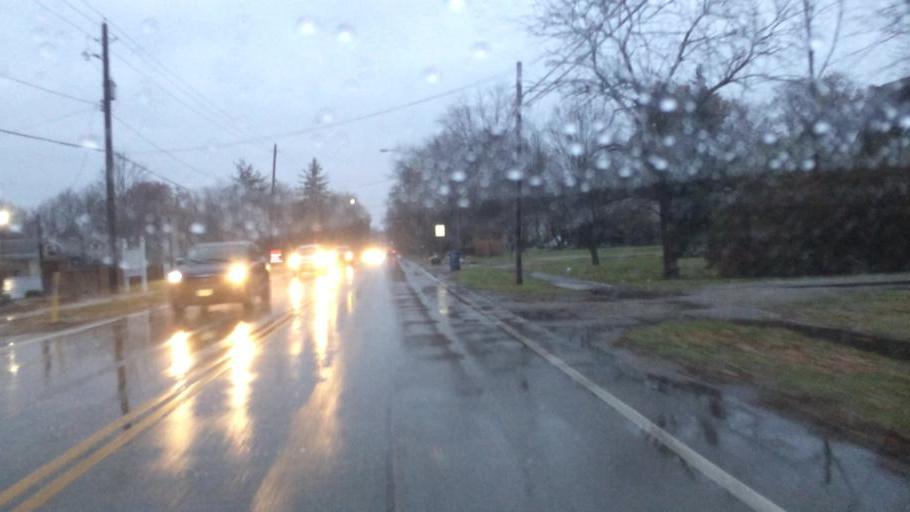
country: US
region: Ohio
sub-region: Cuyahoga County
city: Olmsted Falls
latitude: 41.3825
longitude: -81.9030
